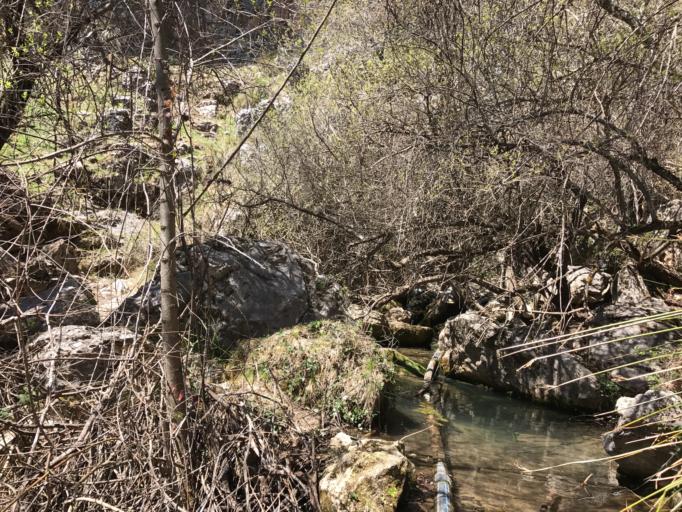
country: ES
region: Andalusia
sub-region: Provincia de Granada
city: Beas de Granada
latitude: 37.3166
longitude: -3.4551
